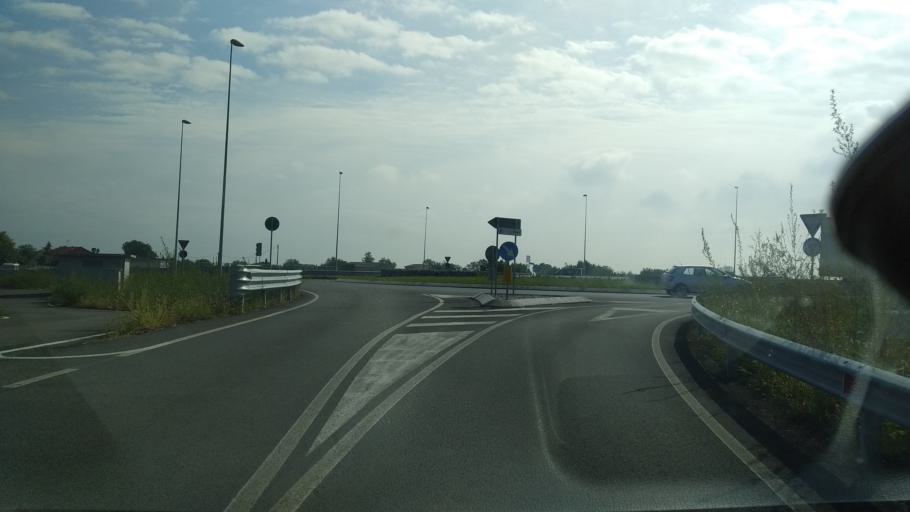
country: IT
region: Veneto
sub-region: Provincia di Vicenza
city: Breganze
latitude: 45.6976
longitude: 11.5780
